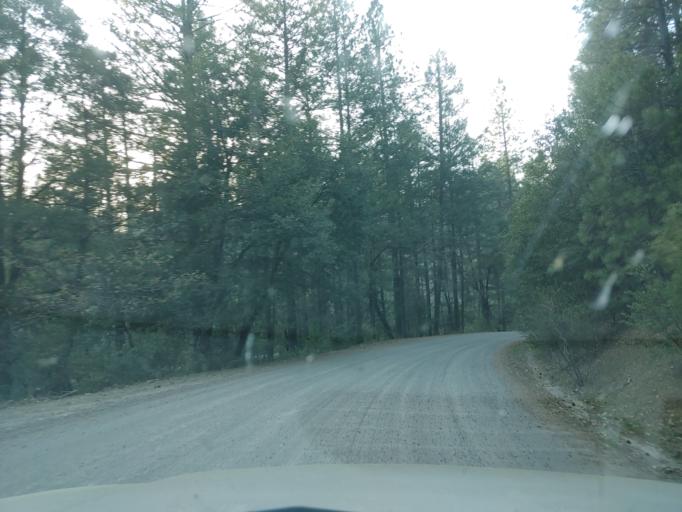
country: US
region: California
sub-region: Shasta County
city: Bella Vista
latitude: 40.8147
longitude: -121.9929
